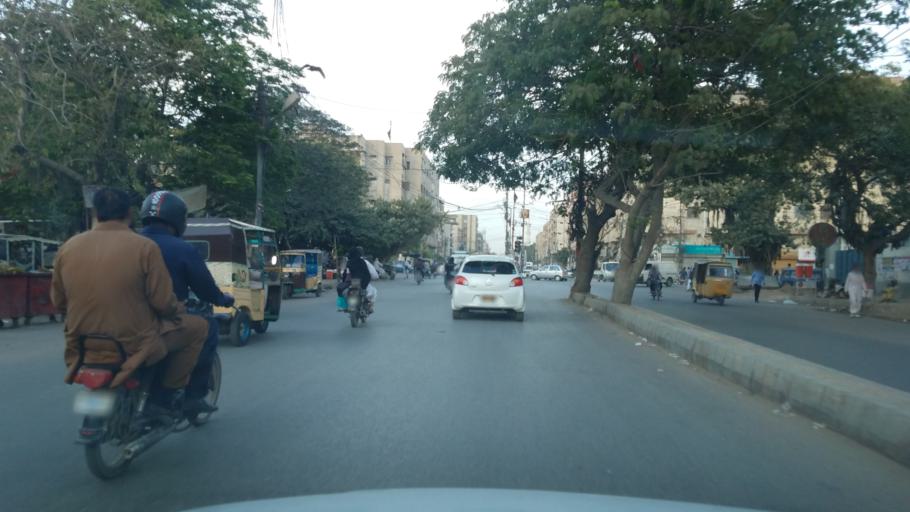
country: PK
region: Sindh
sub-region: Karachi District
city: Karachi
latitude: 24.8768
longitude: 67.0339
